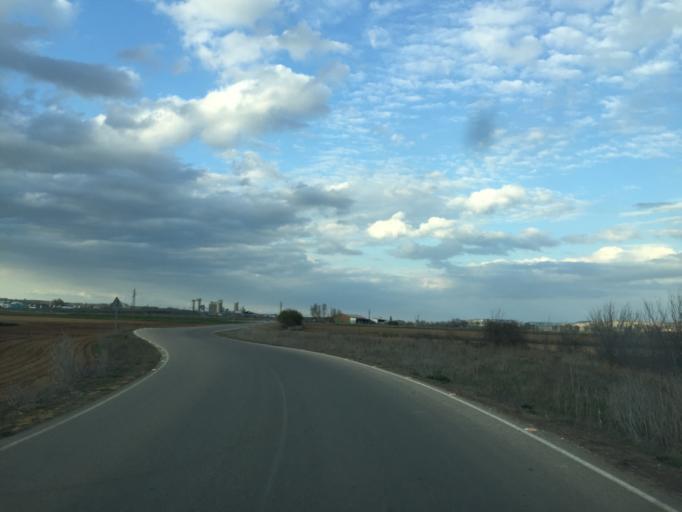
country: ES
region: Castille and Leon
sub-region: Provincia de Palencia
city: Venta de Banos
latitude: 41.9236
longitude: -4.4825
